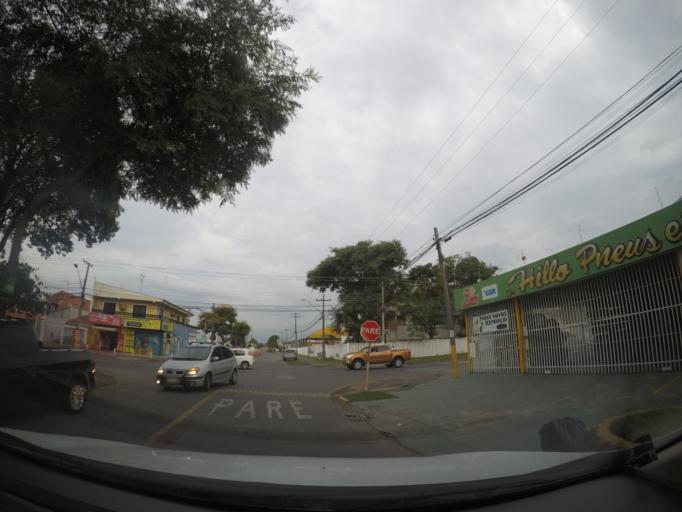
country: BR
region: Parana
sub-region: Sao Jose Dos Pinhais
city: Sao Jose dos Pinhais
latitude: -25.5236
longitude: -49.2336
